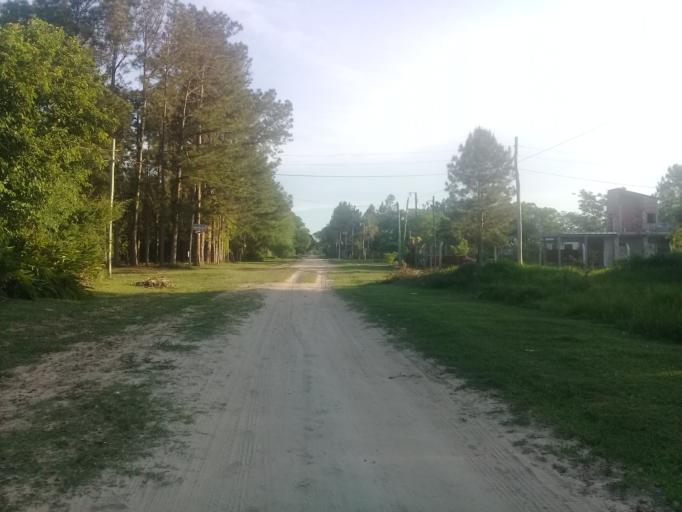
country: AR
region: Corrientes
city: San Luis del Palmar
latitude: -27.4486
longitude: -58.6553
